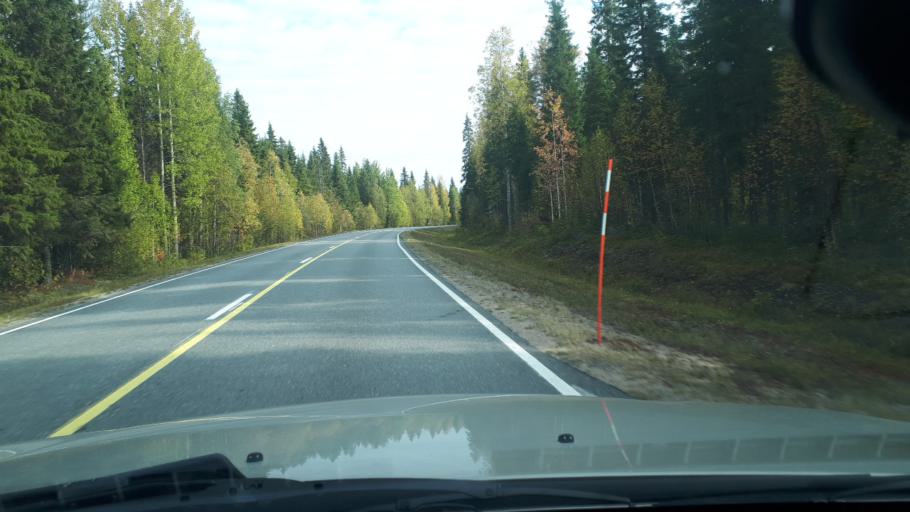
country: FI
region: Northern Ostrobothnia
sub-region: Oulu
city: Yli-Ii
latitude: 65.9501
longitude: 25.9094
